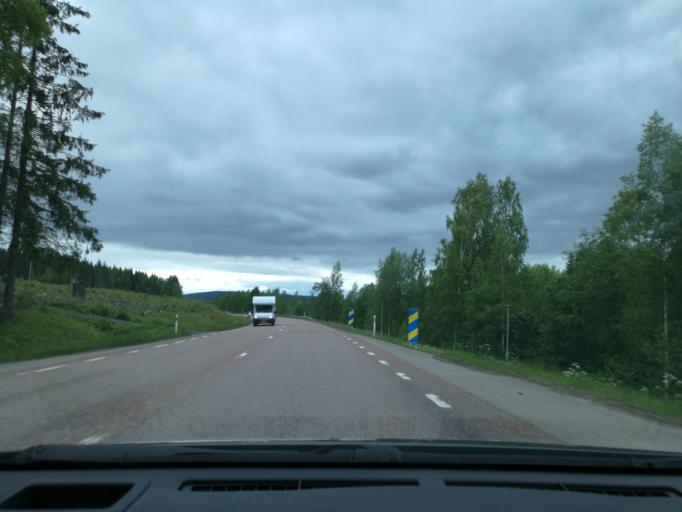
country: SE
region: Dalarna
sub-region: Smedjebackens Kommun
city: Smedjebacken
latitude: 60.1238
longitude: 15.4711
